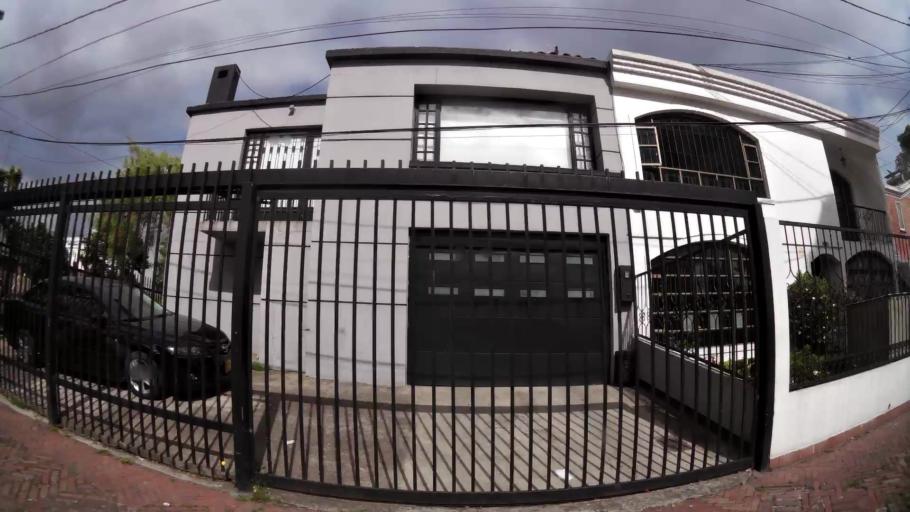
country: CO
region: Bogota D.C.
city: Barrio San Luis
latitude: 4.6914
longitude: -74.0580
